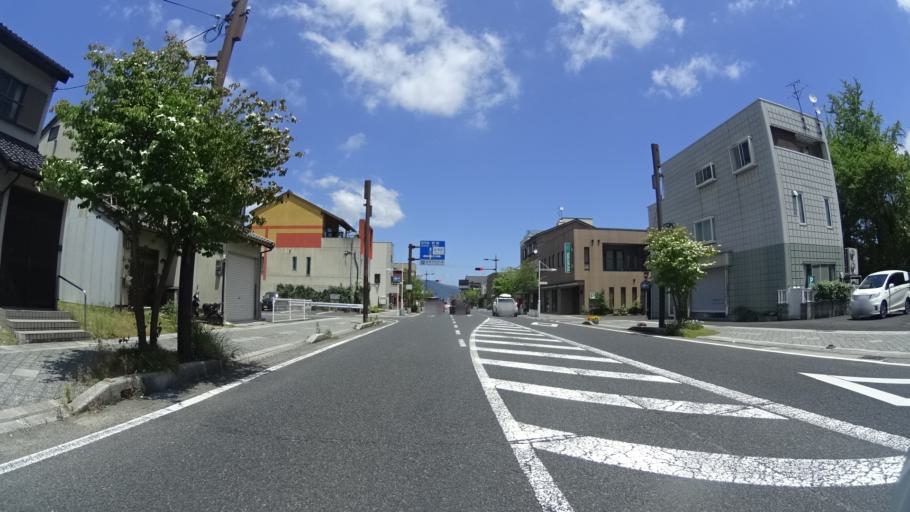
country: JP
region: Kyoto
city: Miyazu
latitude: 35.5354
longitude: 135.1936
